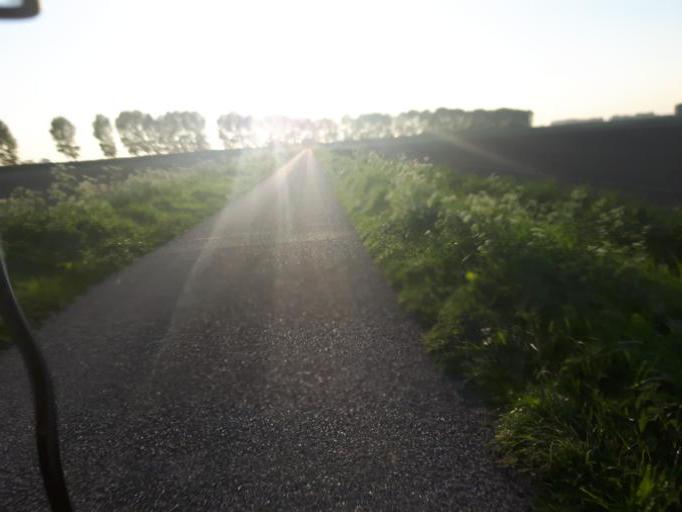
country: NL
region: Zeeland
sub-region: Gemeente Goes
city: Goes
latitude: 51.5097
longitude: 3.8116
